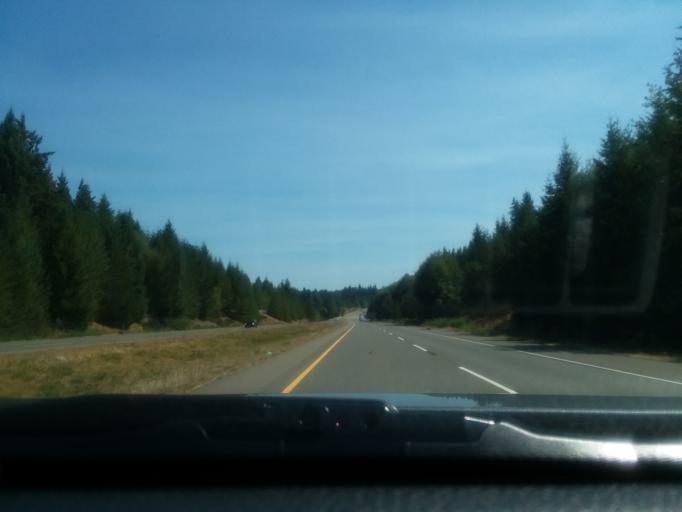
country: CA
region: British Columbia
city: Port Alberni
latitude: 49.3896
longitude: -124.6392
